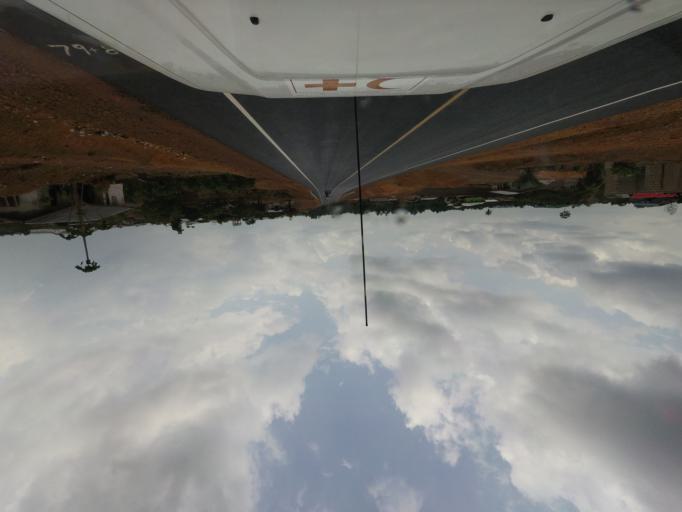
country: LR
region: Margibi
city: Kakata
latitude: 6.6980
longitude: -10.1968
